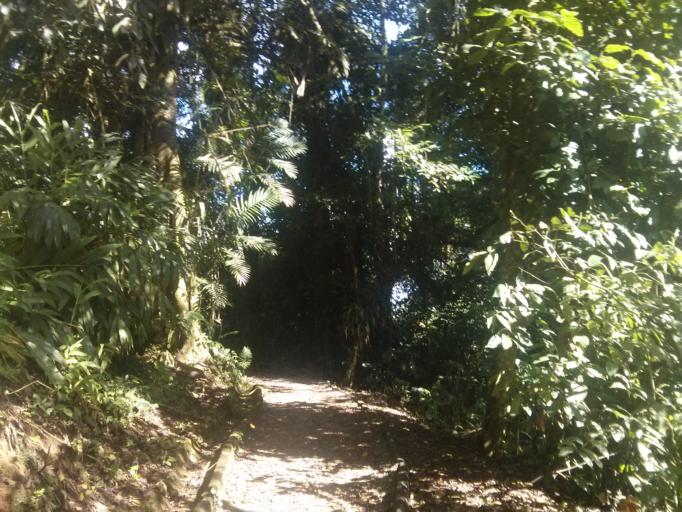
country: CR
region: Cartago
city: Turrialba
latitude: 9.9727
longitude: -83.6923
